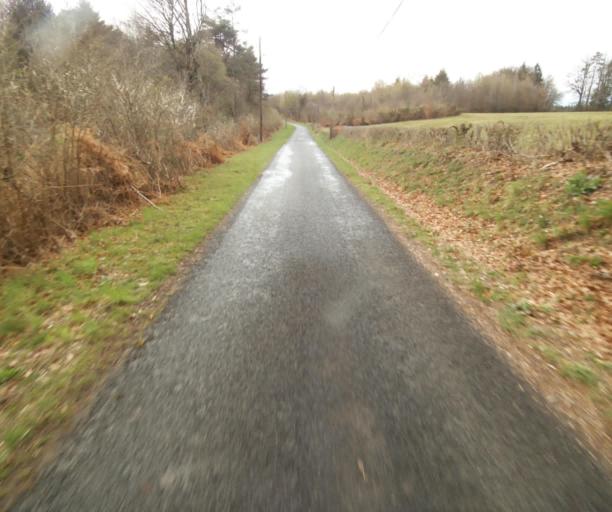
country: FR
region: Limousin
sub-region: Departement de la Correze
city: Saint-Privat
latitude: 45.2232
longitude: 2.0144
